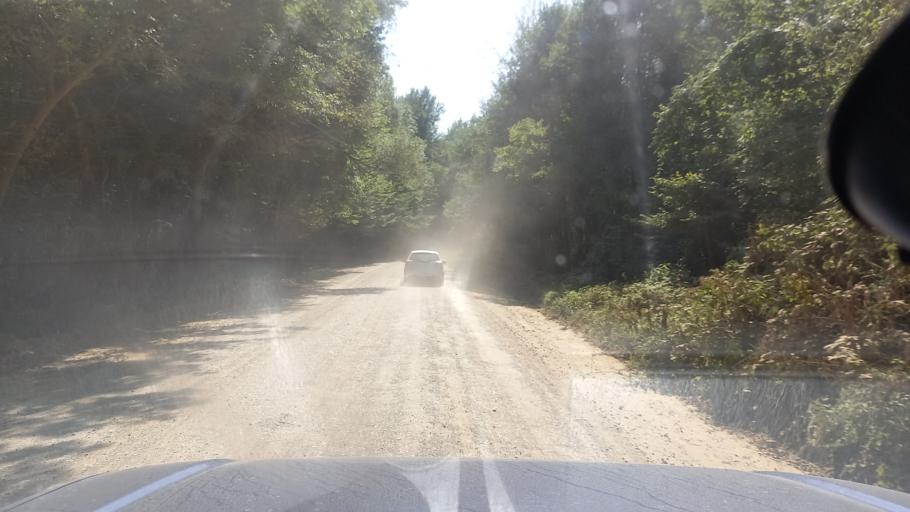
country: RU
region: Krasnodarskiy
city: Azovskaya
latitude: 44.6853
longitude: 38.6385
